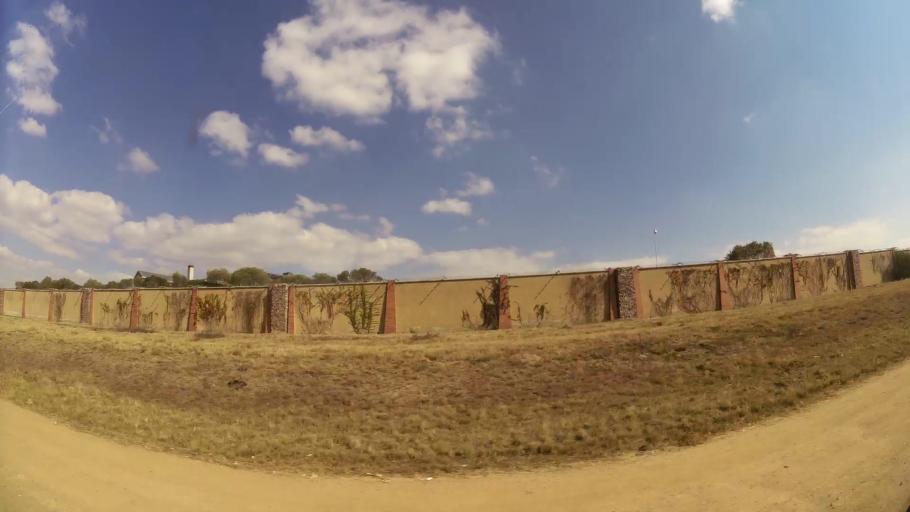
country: ZA
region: Gauteng
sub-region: City of Johannesburg Metropolitan Municipality
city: Midrand
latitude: -26.0166
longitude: 28.0845
